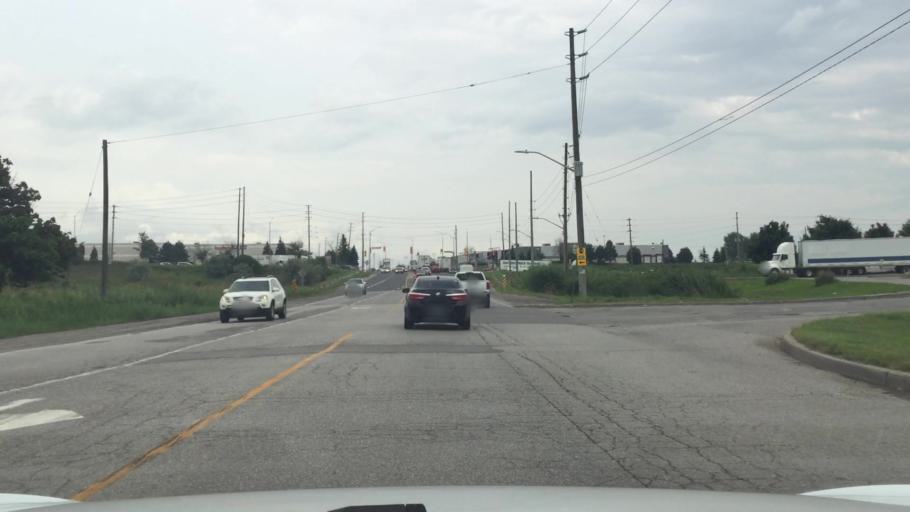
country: CA
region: Ontario
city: Oshawa
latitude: 43.8651
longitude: -78.9066
